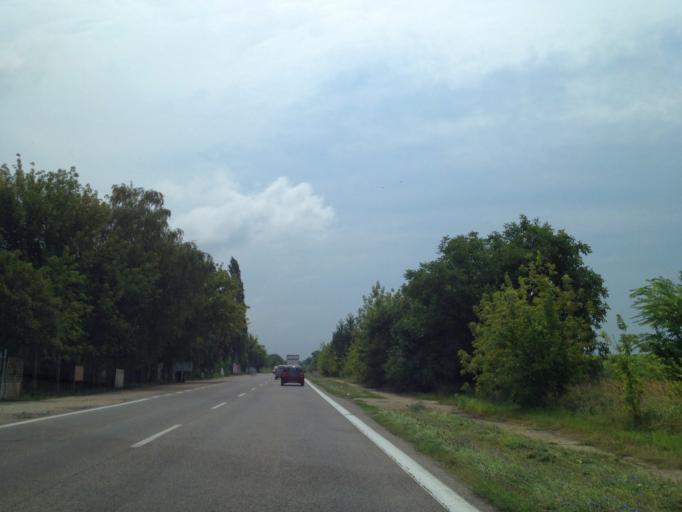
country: SK
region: Nitriansky
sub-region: Okres Nove Zamky
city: Sturovo
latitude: 47.7944
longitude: 18.6945
